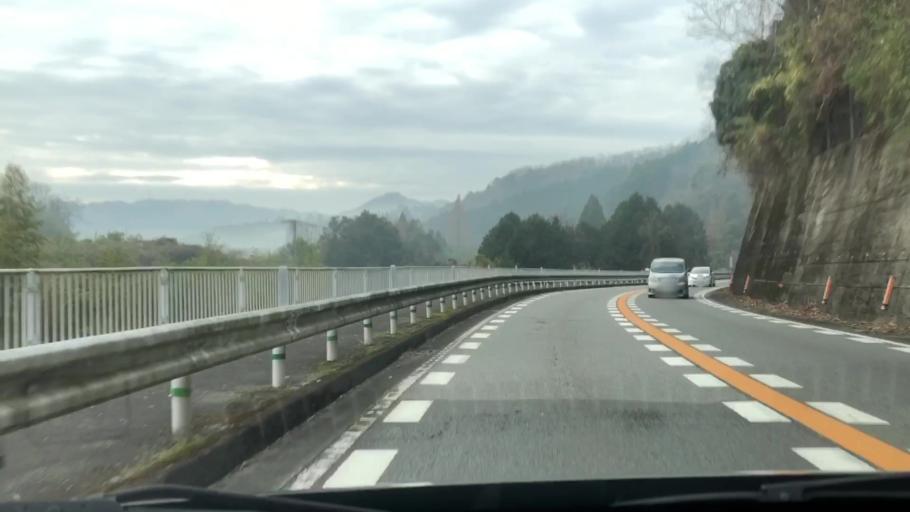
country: JP
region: Oita
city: Usuki
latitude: 33.0263
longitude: 131.6945
